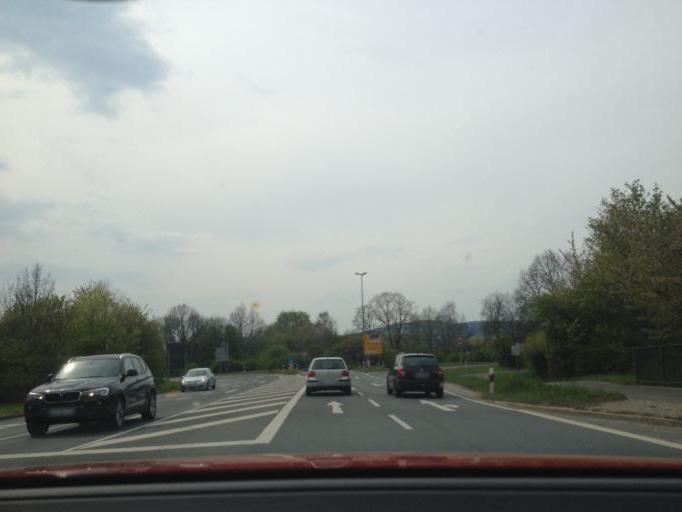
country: DE
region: Bavaria
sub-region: Upper Franconia
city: Bindlach
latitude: 49.9634
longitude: 11.6114
